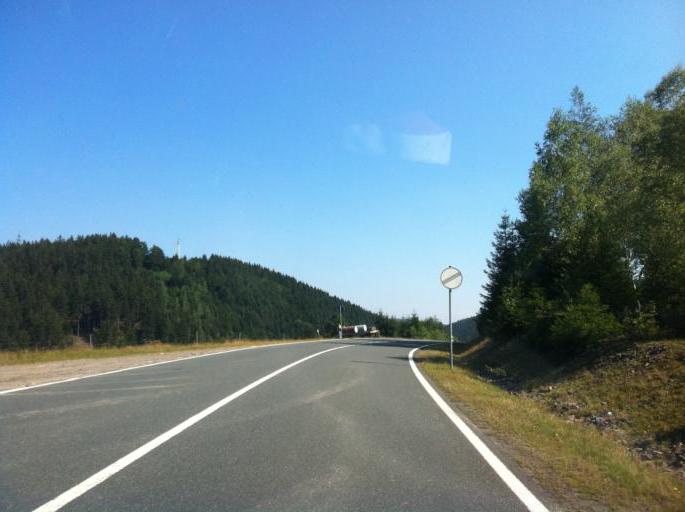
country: DE
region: Thuringia
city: Goldisthal
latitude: 50.5209
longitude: 11.0081
